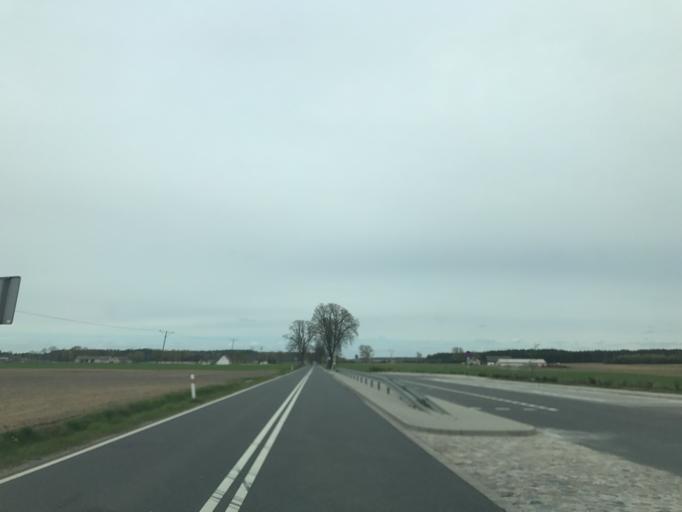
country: PL
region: Warmian-Masurian Voivodeship
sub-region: Powiat dzialdowski
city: Lidzbark
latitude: 53.3627
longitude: 19.8192
